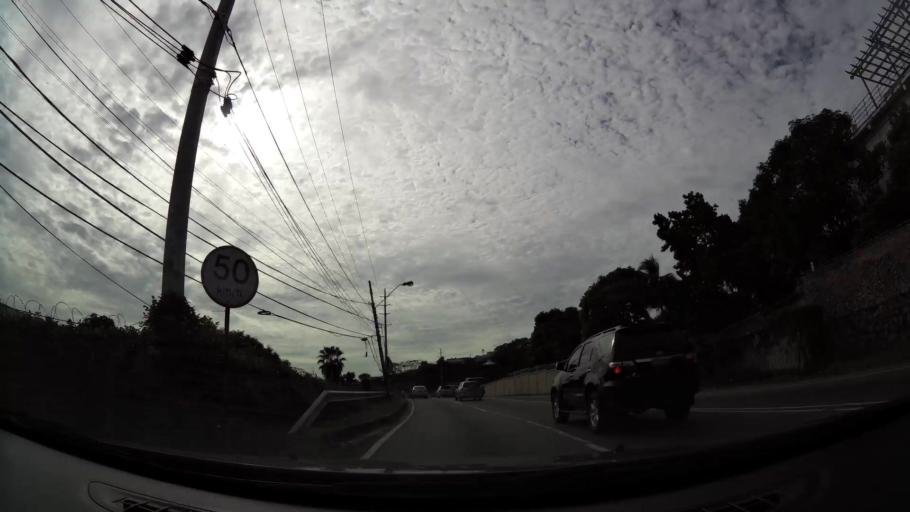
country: TT
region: City of Port of Spain
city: Mucurapo
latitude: 10.6821
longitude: -61.5639
